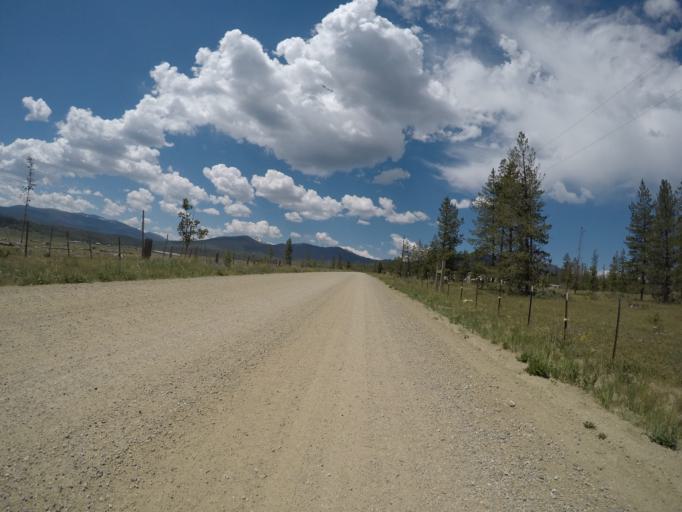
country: US
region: Colorado
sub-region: Grand County
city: Fraser
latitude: 39.9644
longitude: -105.8636
